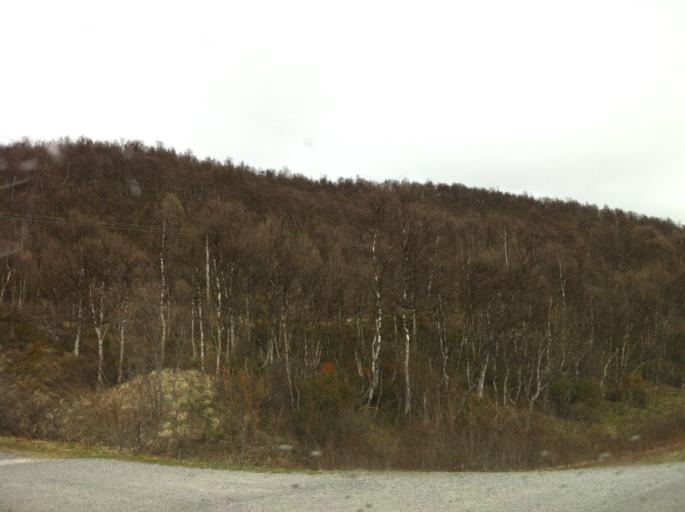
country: NO
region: Sor-Trondelag
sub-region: Tydal
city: Aas
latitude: 62.5852
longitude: 12.1997
